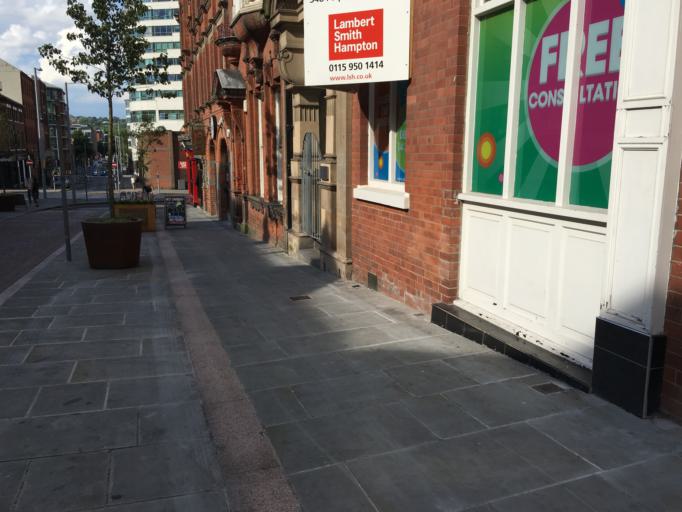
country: GB
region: England
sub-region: Nottingham
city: Nottingham
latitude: 52.9548
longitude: -1.1432
